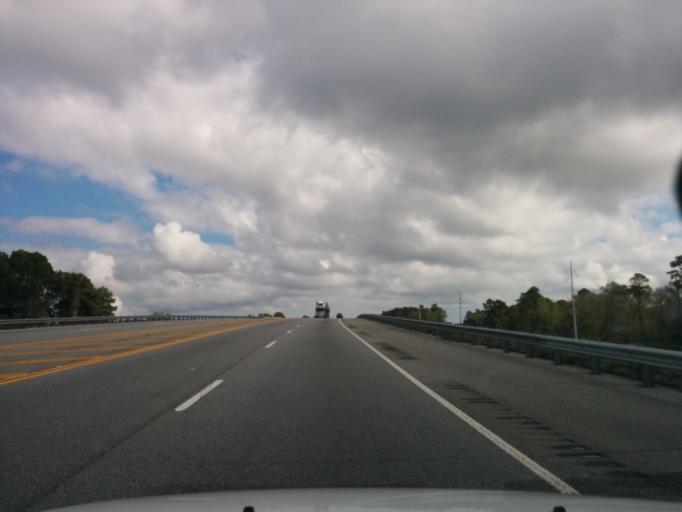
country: US
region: Georgia
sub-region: Glynn County
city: Brunswick
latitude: 31.1223
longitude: -81.5450
